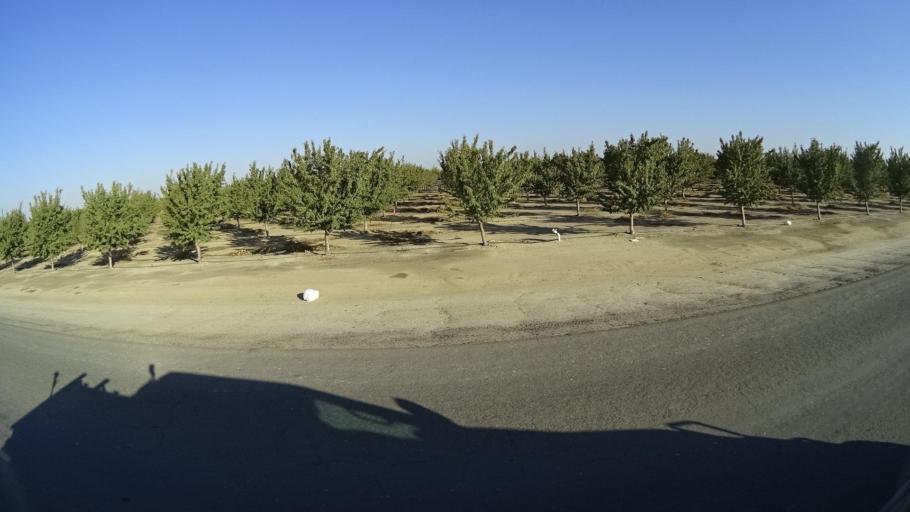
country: US
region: California
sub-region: Kern County
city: Delano
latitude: 35.7687
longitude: -119.2109
